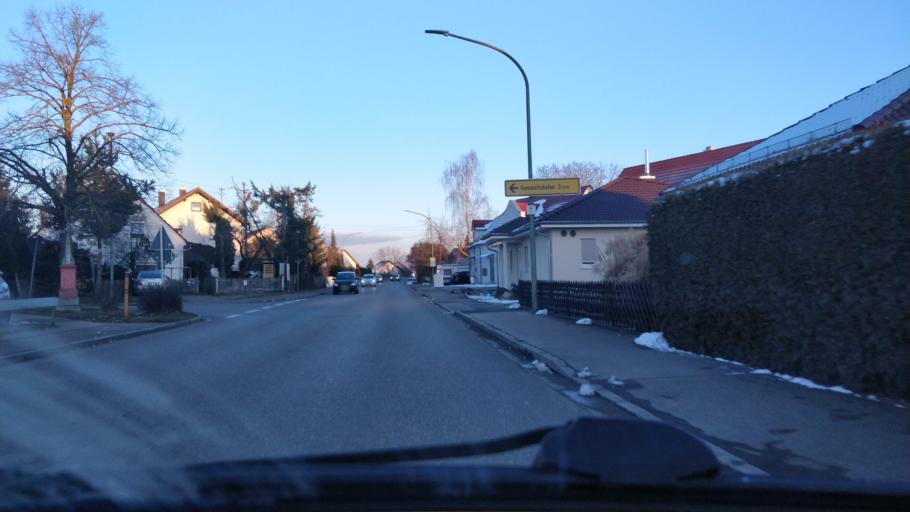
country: DE
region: Bavaria
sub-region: Swabia
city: Holzheim
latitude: 48.3795
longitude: 10.1068
